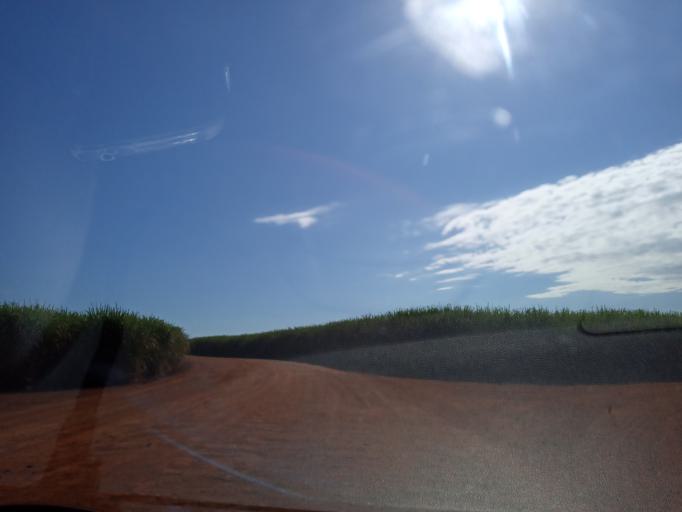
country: BR
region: Goias
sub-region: Itumbiara
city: Itumbiara
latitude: -18.4496
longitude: -49.1790
